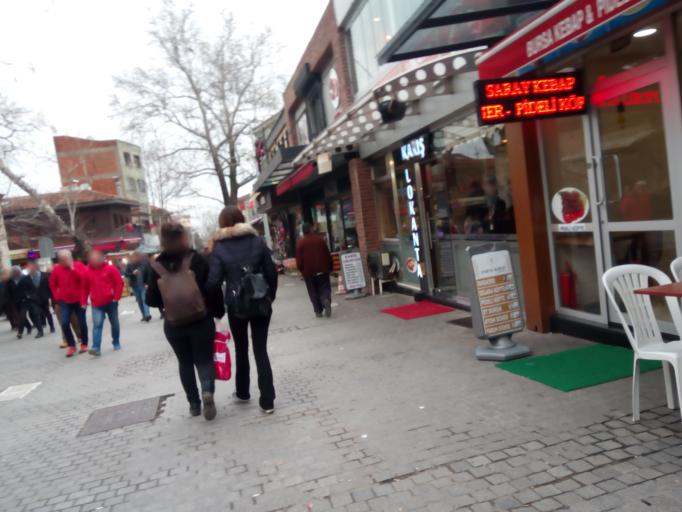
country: TR
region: Bursa
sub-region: Osmangazi
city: Bursa
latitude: 40.1857
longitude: 29.0611
